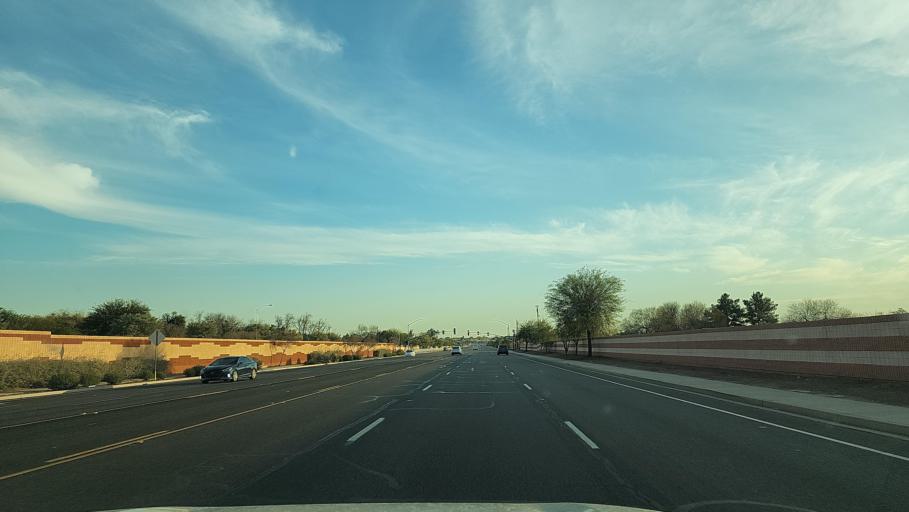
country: US
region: Arizona
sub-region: Maricopa County
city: Mesa
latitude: 33.4756
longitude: -111.7875
